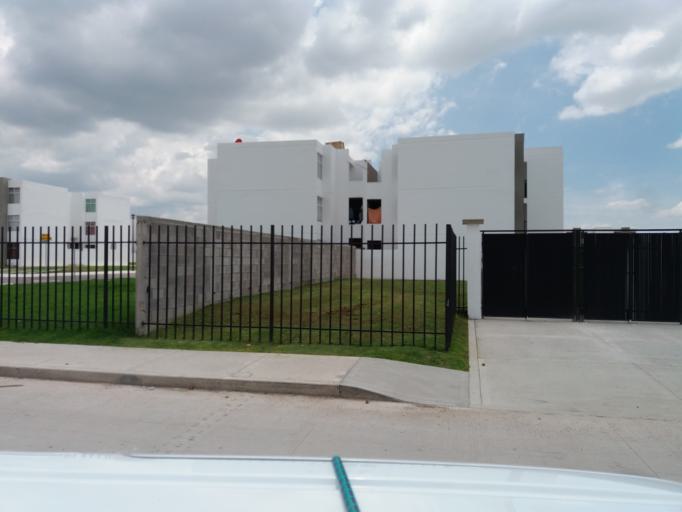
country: MX
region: Aguascalientes
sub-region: Aguascalientes
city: San Sebastian [Fraccionamiento]
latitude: 21.8052
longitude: -102.2754
